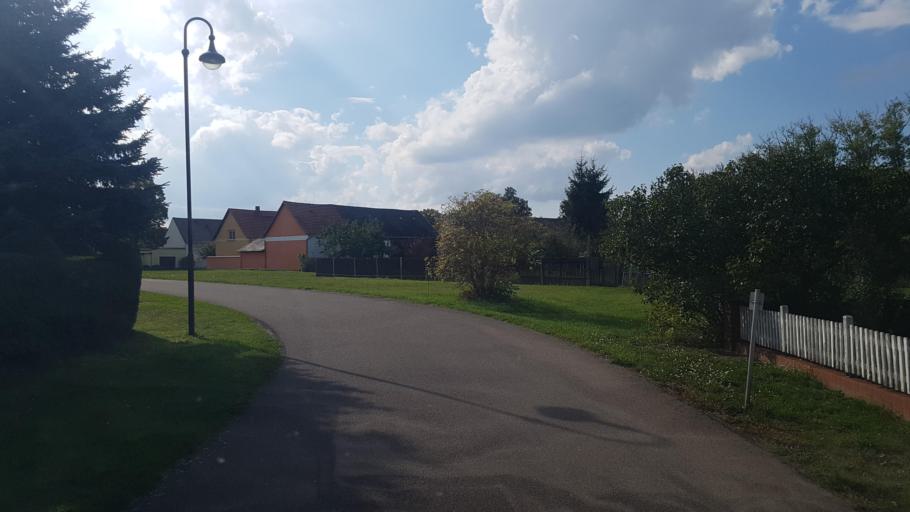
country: DE
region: Brandenburg
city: Ihlow
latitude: 51.8808
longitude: 13.3526
